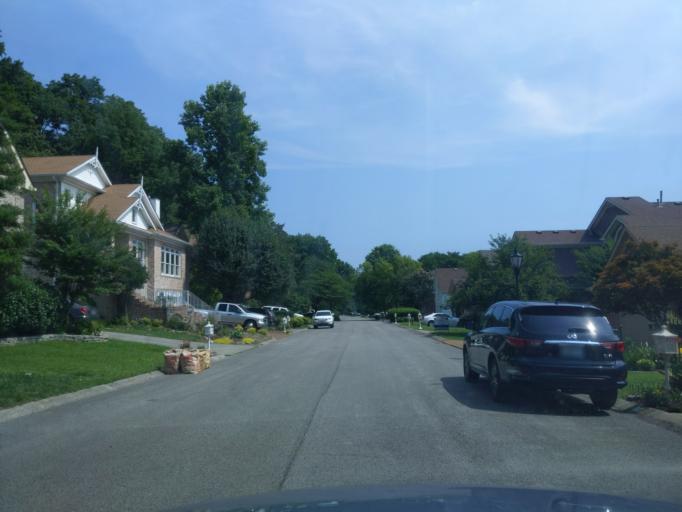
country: US
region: Tennessee
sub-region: Williamson County
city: Brentwood Estates
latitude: 36.0352
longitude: -86.7491
